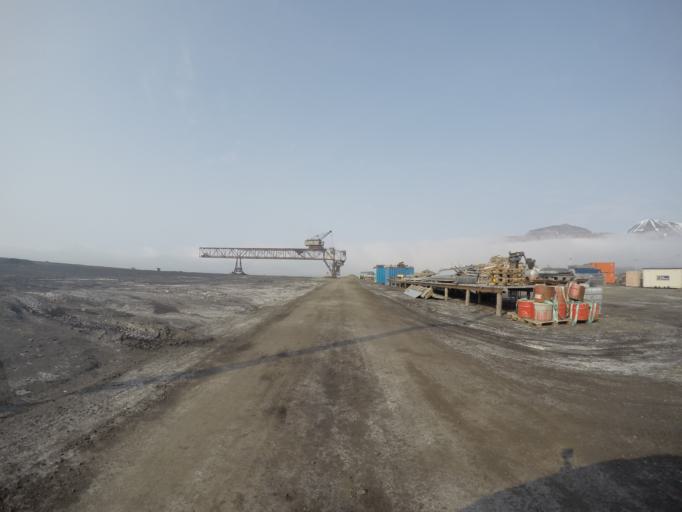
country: SJ
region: Svalbard
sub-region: Spitsbergen
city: Longyearbyen
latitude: 78.2450
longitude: 15.5404
